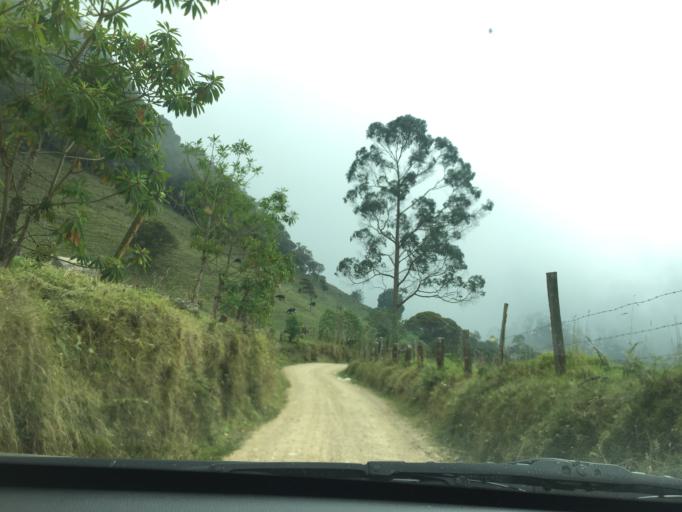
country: CO
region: Cundinamarca
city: Bojaca
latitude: 4.7072
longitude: -74.3589
